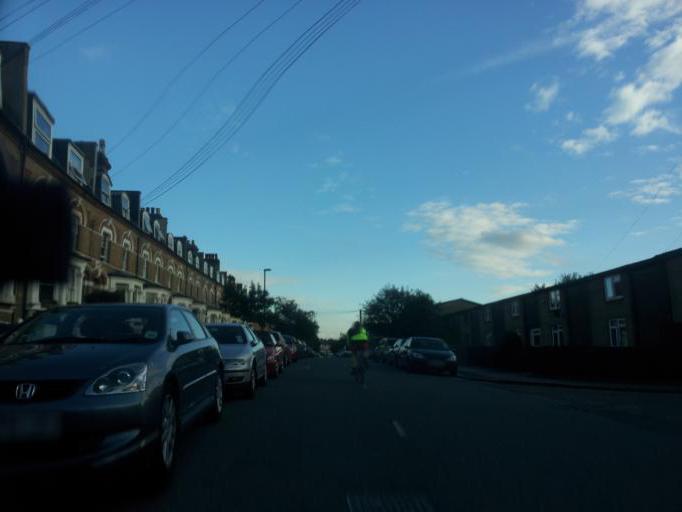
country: GB
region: England
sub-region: Greater London
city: Beckenham
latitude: 51.4260
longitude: -0.0541
